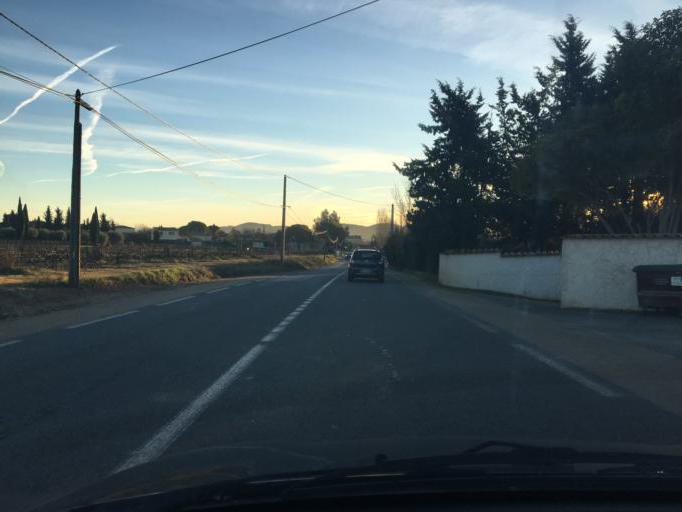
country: FR
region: Provence-Alpes-Cote d'Azur
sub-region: Departement du Var
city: Les Arcs
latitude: 43.4493
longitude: 6.4714
